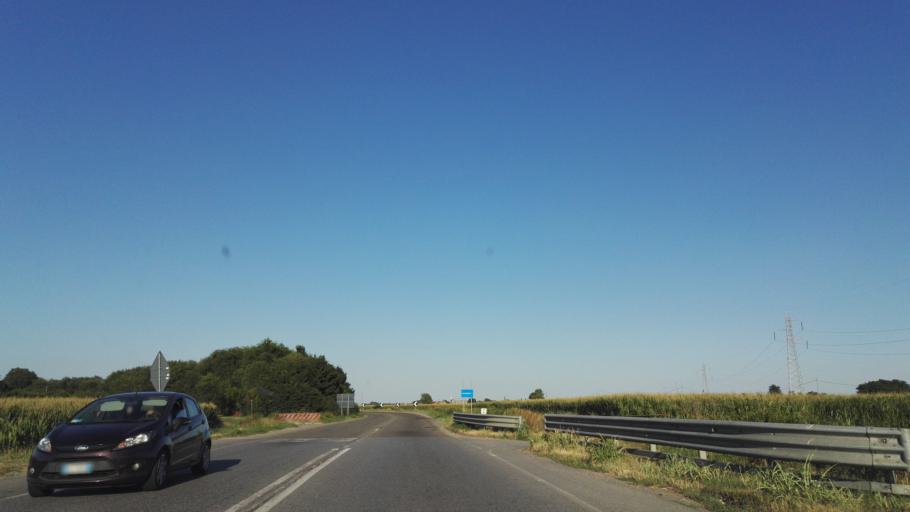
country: IT
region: Lombardy
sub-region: Citta metropolitana di Milano
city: Locate di Triulzi
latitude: 45.3616
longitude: 9.2373
